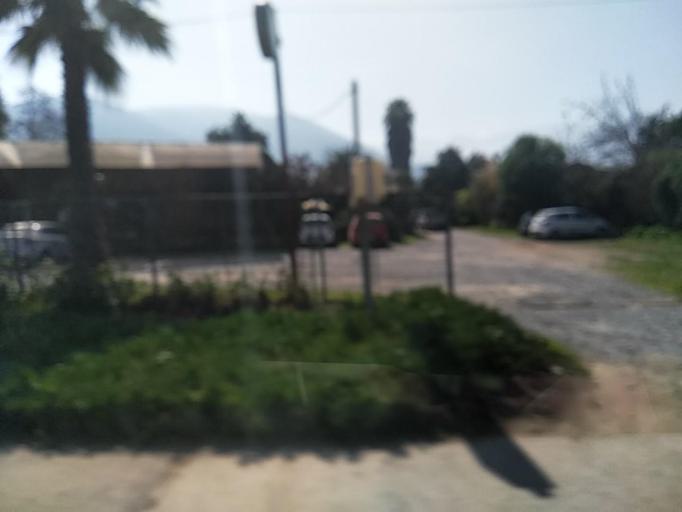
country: CL
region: Santiago Metropolitan
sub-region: Provincia de Chacabuco
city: Lampa
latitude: -33.4089
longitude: -71.0667
